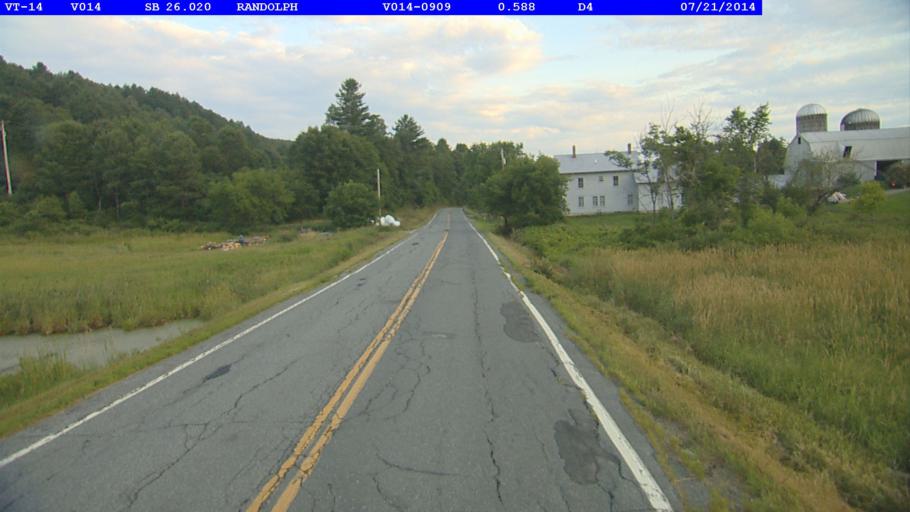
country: US
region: Vermont
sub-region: Orange County
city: Randolph
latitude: 43.8842
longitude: -72.5813
